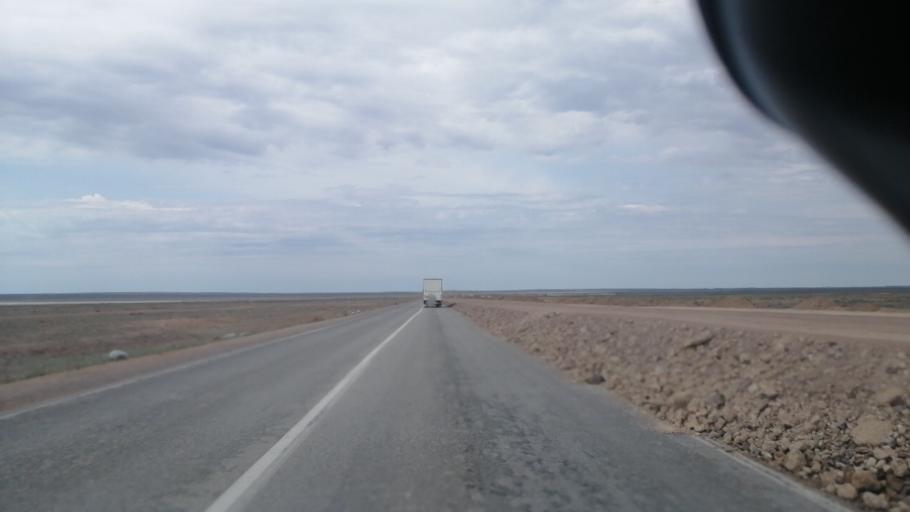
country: KZ
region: Qaraghandy
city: Saryshaghan
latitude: 46.4229
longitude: 73.9316
